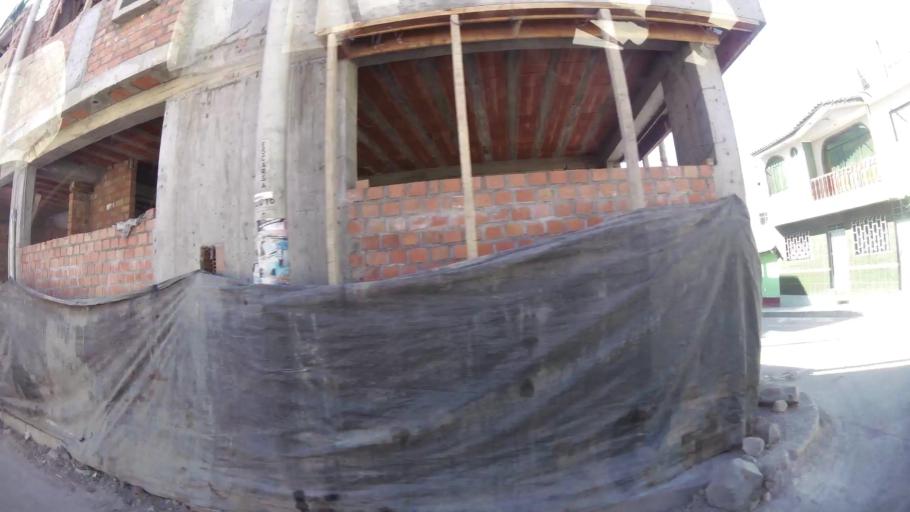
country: PE
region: Ayacucho
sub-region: Provincia de Huamanga
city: Ayacucho
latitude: -13.1615
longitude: -74.2348
